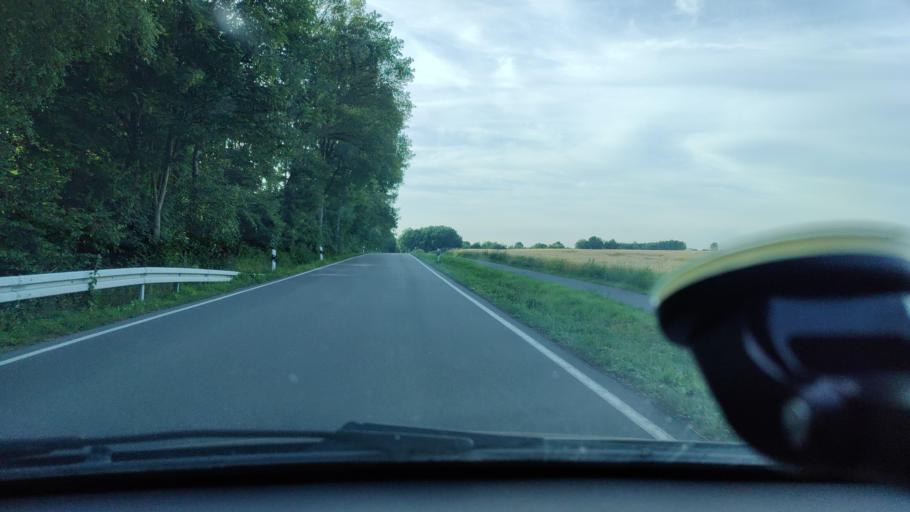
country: DE
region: North Rhine-Westphalia
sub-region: Regierungsbezirk Munster
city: Billerbeck
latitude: 52.0043
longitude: 7.2226
